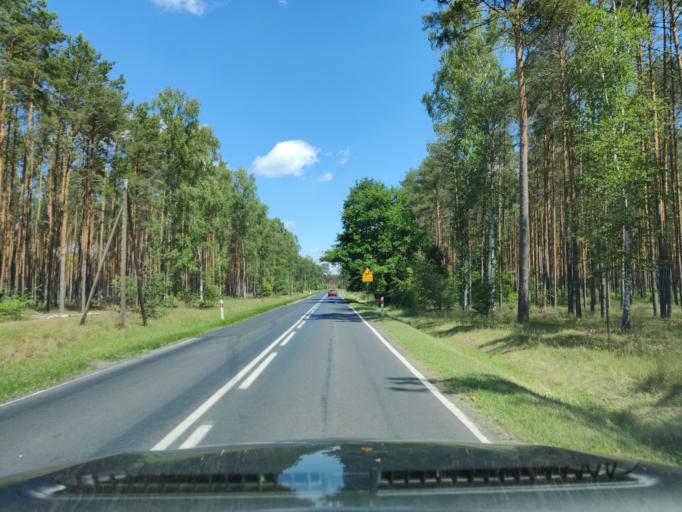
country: PL
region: Greater Poland Voivodeship
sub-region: Powiat nowotomyski
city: Nowy Tomysl
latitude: 52.2245
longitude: 16.1051
